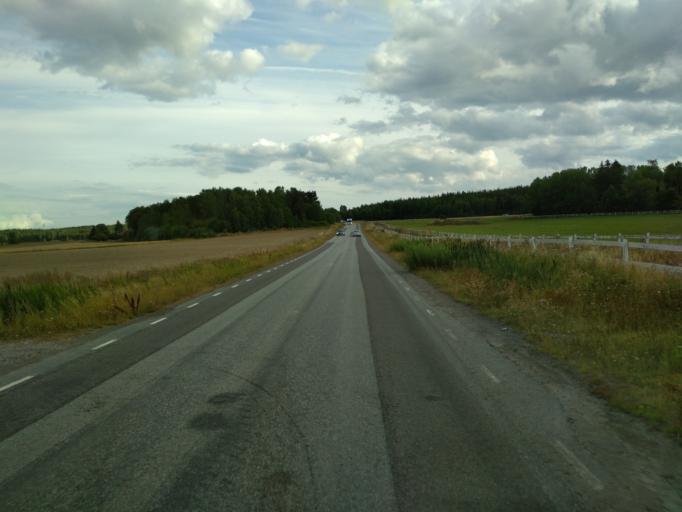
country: SE
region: Uppsala
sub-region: Habo Kommun
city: Balsta
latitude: 59.6594
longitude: 17.5559
